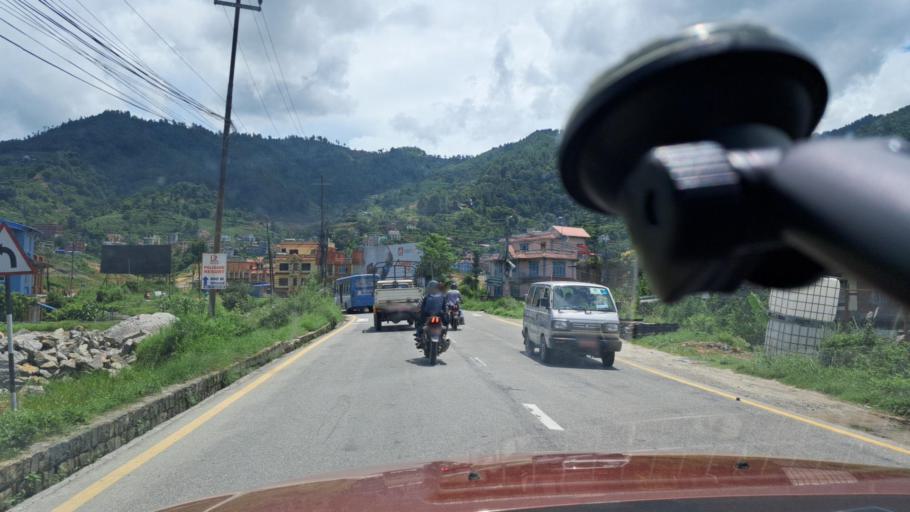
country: NP
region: Central Region
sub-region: Bagmati Zone
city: Hari Bdr Tamang House
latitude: 27.6505
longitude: 85.4623
